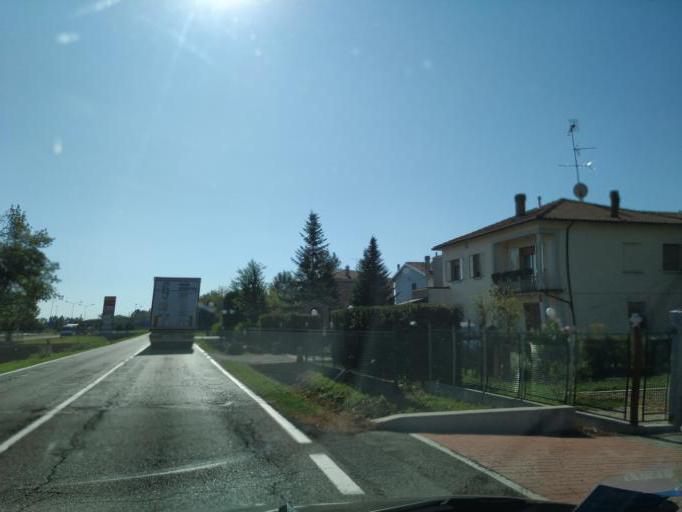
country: IT
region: Emilia-Romagna
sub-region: Provincia di Bologna
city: Sant'Agata Bolognese
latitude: 44.6565
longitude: 11.1360
